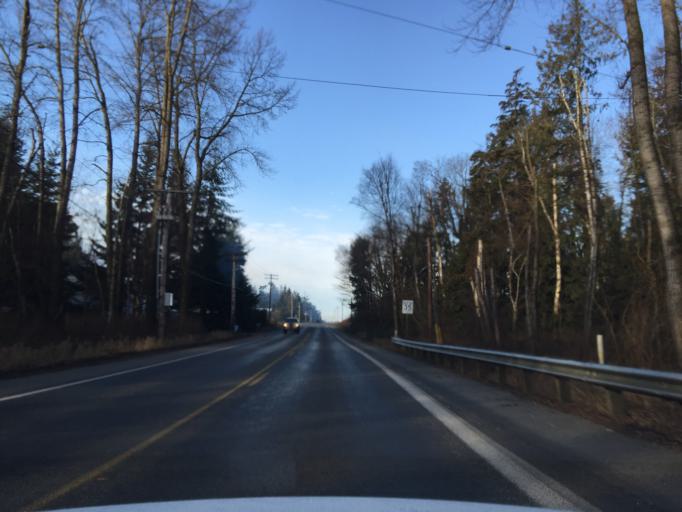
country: US
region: Washington
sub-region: Whatcom County
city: Lynden
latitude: 48.9357
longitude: -122.4964
